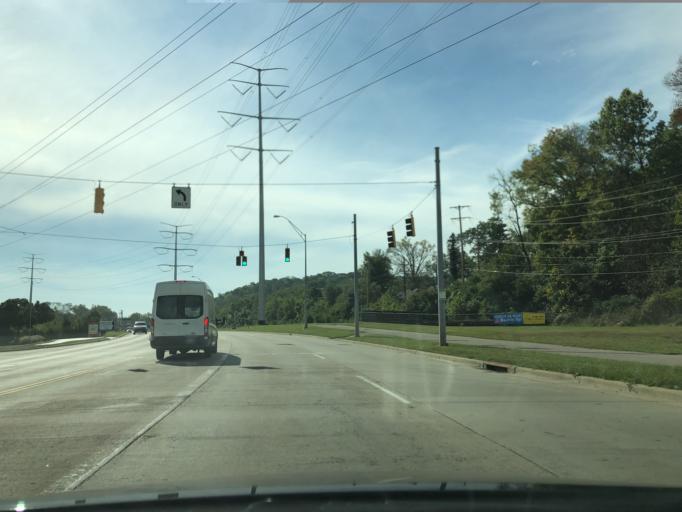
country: US
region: Ohio
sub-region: Hamilton County
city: Fairfax
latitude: 39.1447
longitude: -84.4052
